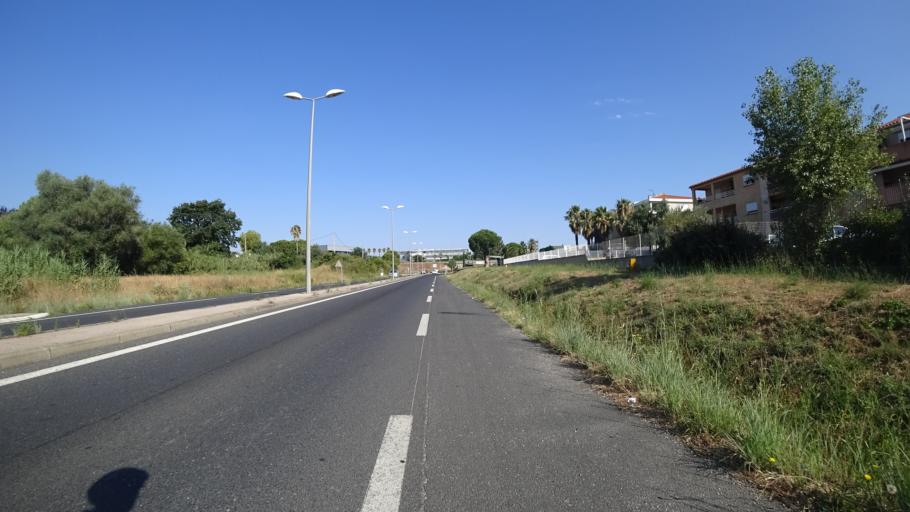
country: FR
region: Languedoc-Roussillon
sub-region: Departement des Pyrenees-Orientales
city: Cabestany
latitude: 42.6987
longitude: 2.9356
